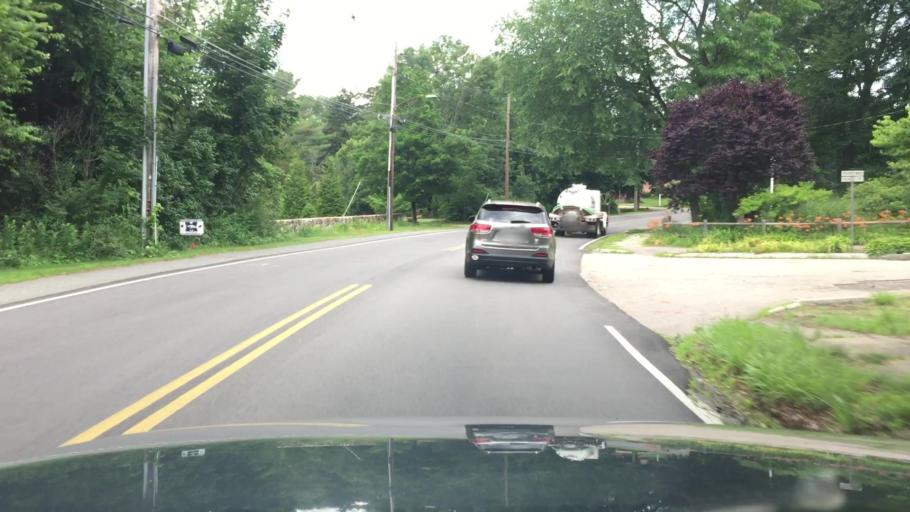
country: US
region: Massachusetts
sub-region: Norfolk County
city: Medway
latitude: 42.1385
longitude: -71.3844
